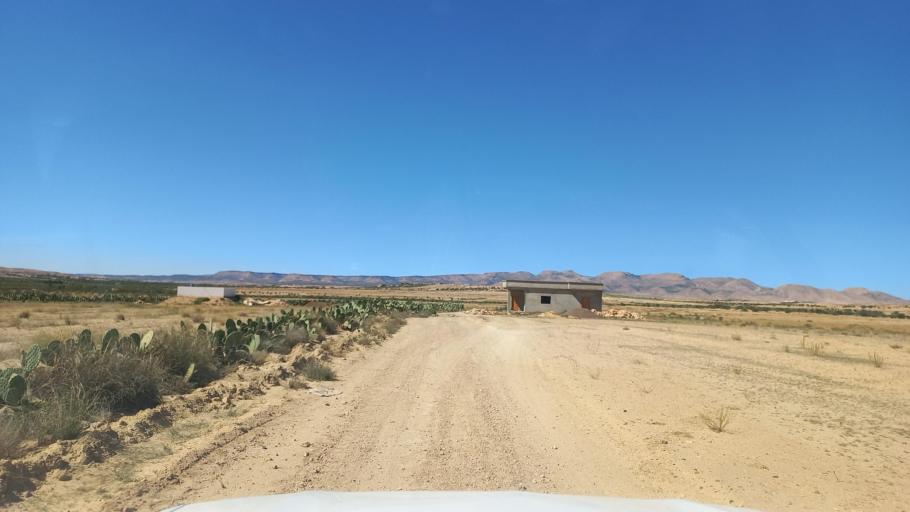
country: TN
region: Al Qasrayn
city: Sbiba
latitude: 35.3684
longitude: 9.0858
